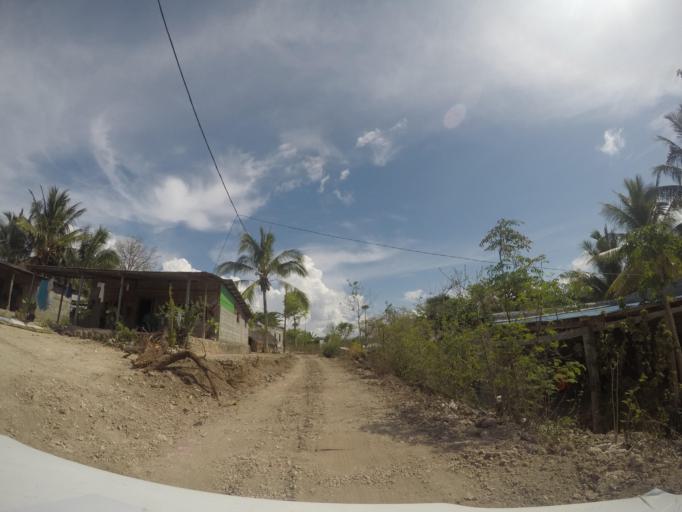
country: TL
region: Baucau
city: Baucau
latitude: -8.4690
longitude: 126.4729
